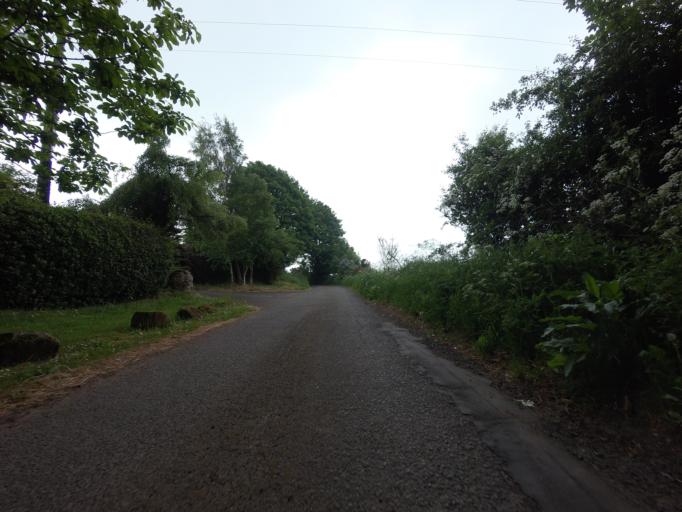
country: GB
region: Scotland
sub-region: Fife
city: Ballingry
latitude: 56.2305
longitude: -3.3433
